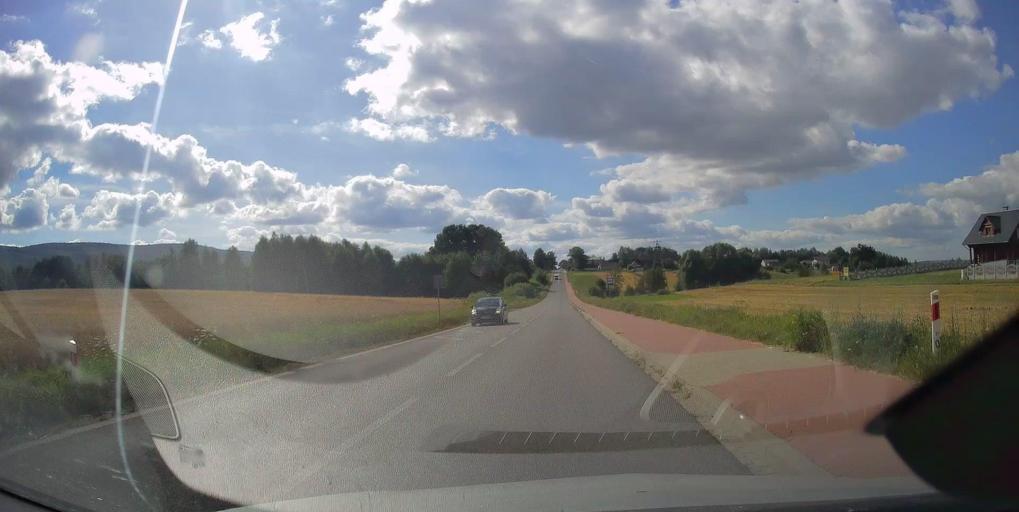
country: PL
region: Swietokrzyskie
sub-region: Powiat kielecki
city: Nowa Slupia
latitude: 50.8815
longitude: 21.0578
